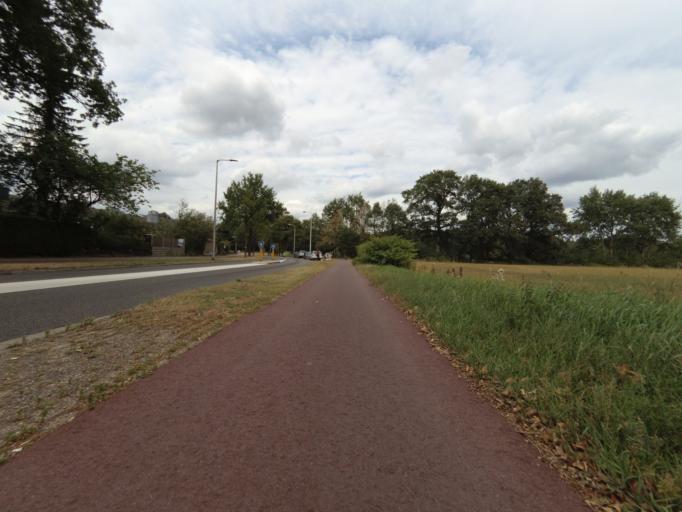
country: NL
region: Overijssel
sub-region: Gemeente Enschede
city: Enschede
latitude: 52.2251
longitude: 6.9290
